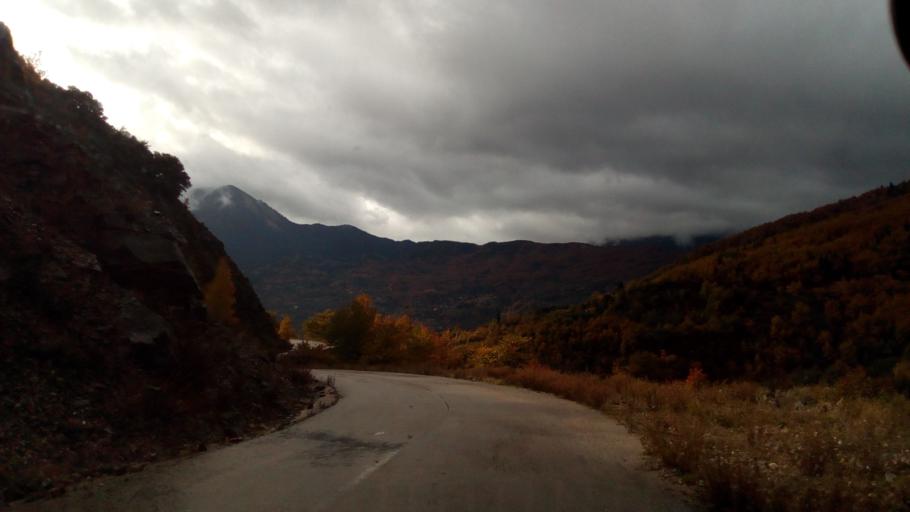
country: GR
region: West Greece
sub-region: Nomos Aitolias kai Akarnanias
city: Thermo
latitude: 38.6836
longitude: 21.8486
